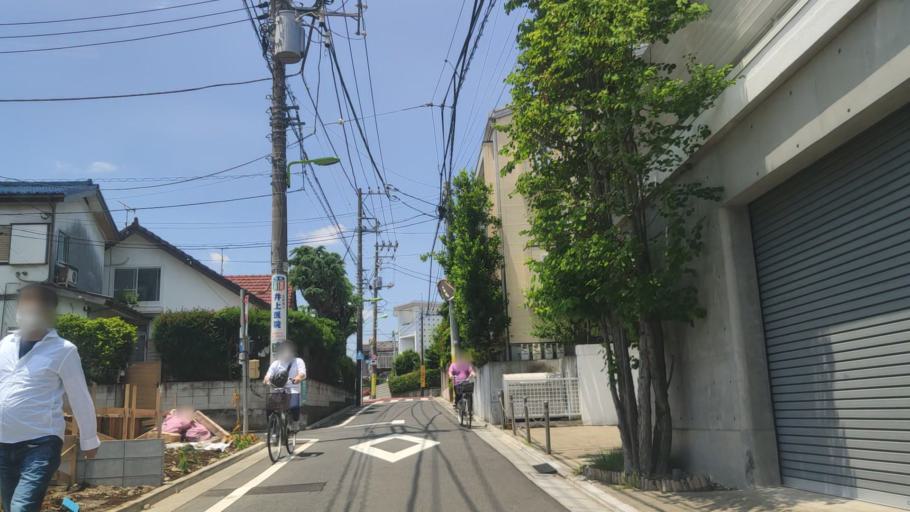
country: JP
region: Tokyo
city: Tokyo
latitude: 35.6607
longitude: 139.6509
